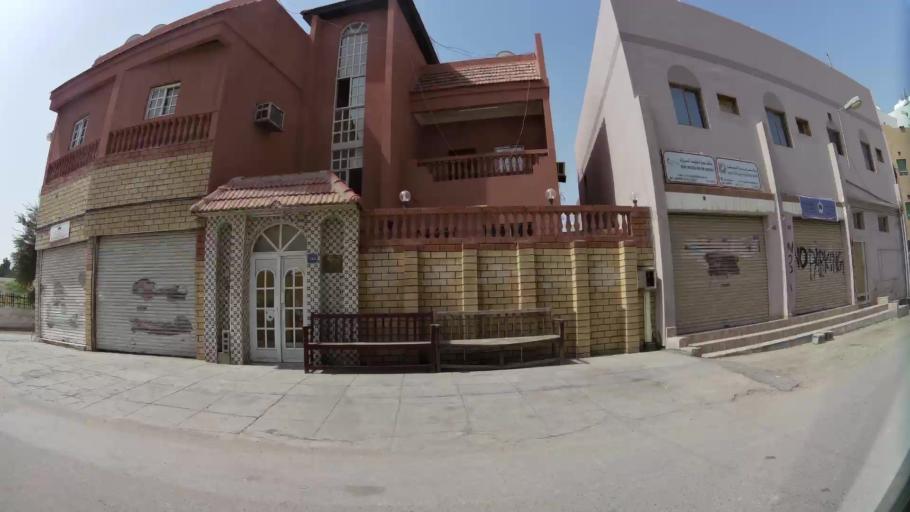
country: BH
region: Manama
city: Jidd Hafs
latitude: 26.2291
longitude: 50.4944
